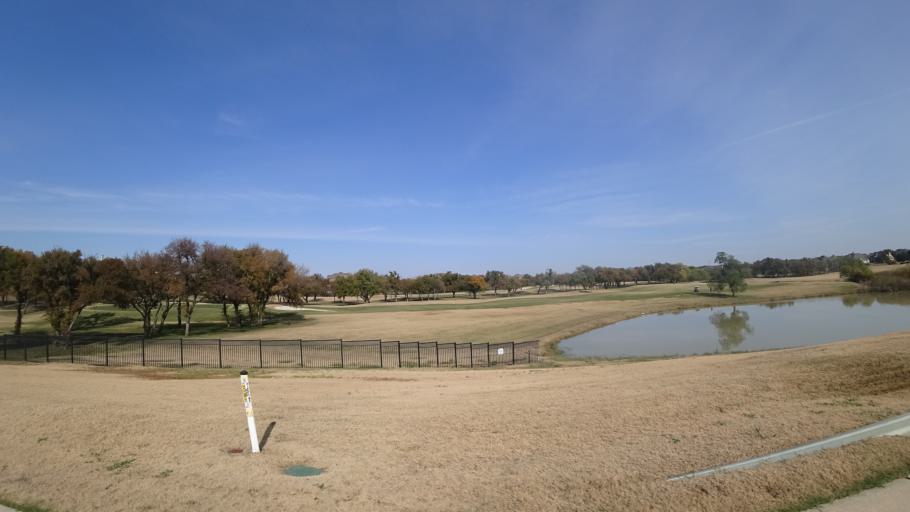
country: US
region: Texas
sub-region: Denton County
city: The Colony
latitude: 33.0407
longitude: -96.9030
